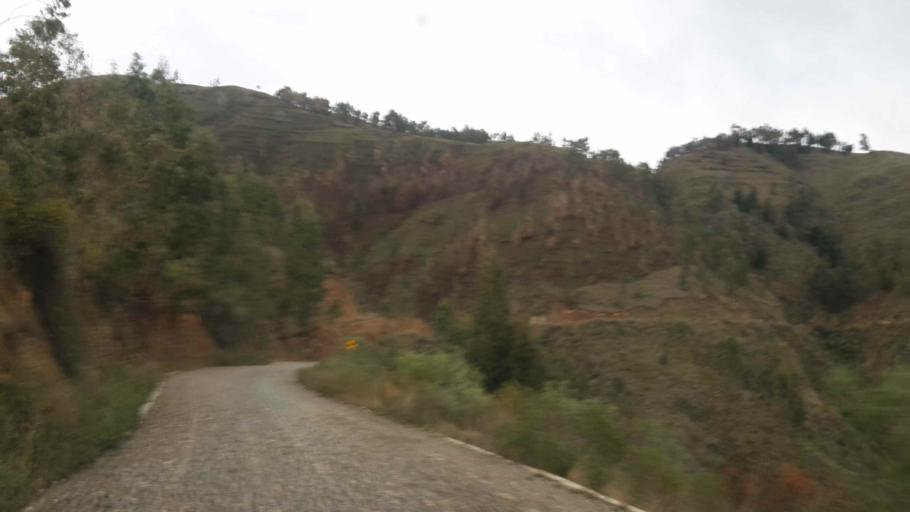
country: BO
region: Cochabamba
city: Cochabamba
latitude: -17.3635
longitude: -66.0617
